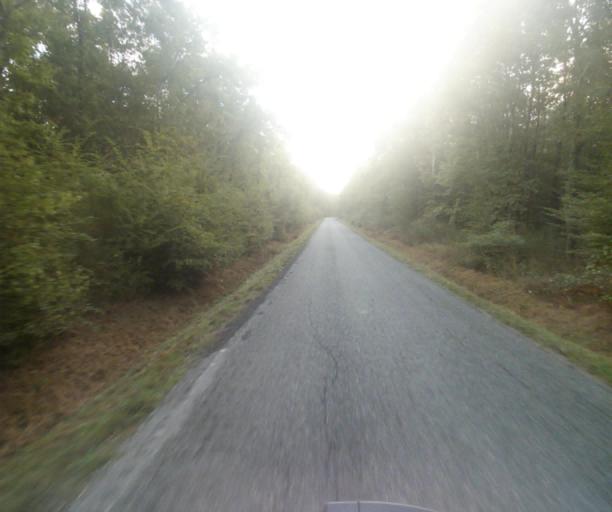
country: FR
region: Midi-Pyrenees
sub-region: Departement du Tarn-et-Garonne
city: Montech
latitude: 43.9389
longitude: 1.2678
